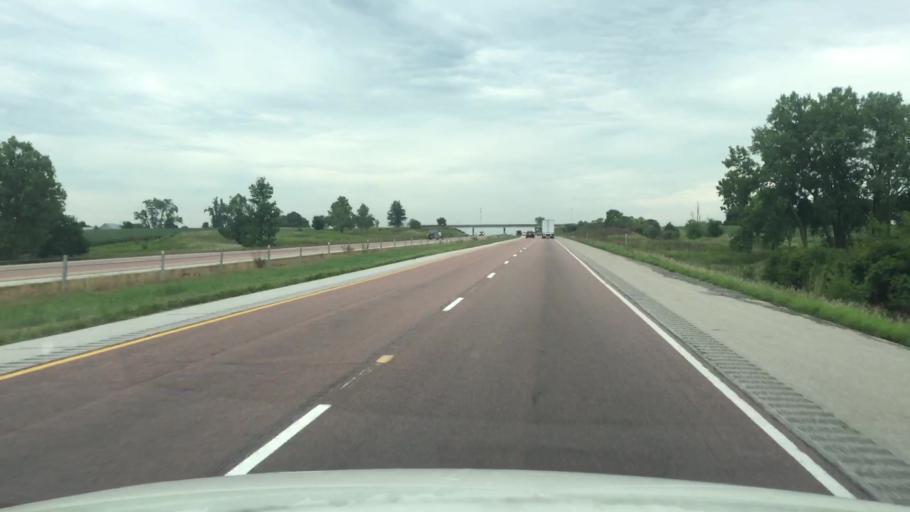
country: US
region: Iowa
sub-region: Clarke County
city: Osceola
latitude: 41.2578
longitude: -93.7808
